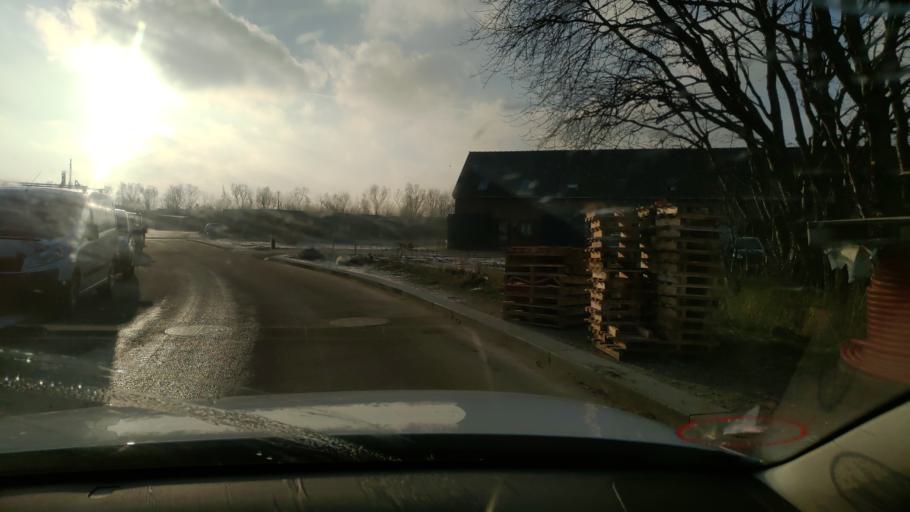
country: DK
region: Zealand
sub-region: Solrod Kommune
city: Solrod Strand
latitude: 55.5456
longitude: 12.2241
